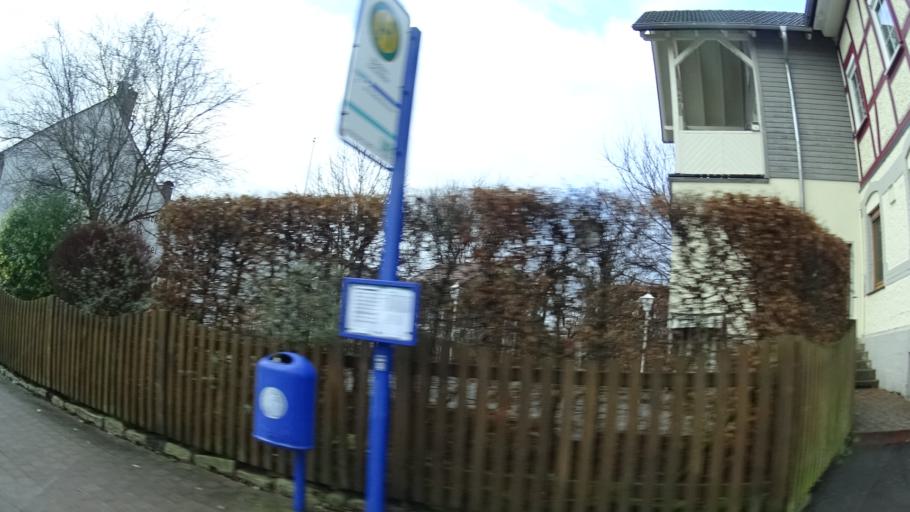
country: DE
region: Hesse
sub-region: Regierungsbezirk Kassel
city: Flieden
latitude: 50.4069
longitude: 9.5802
